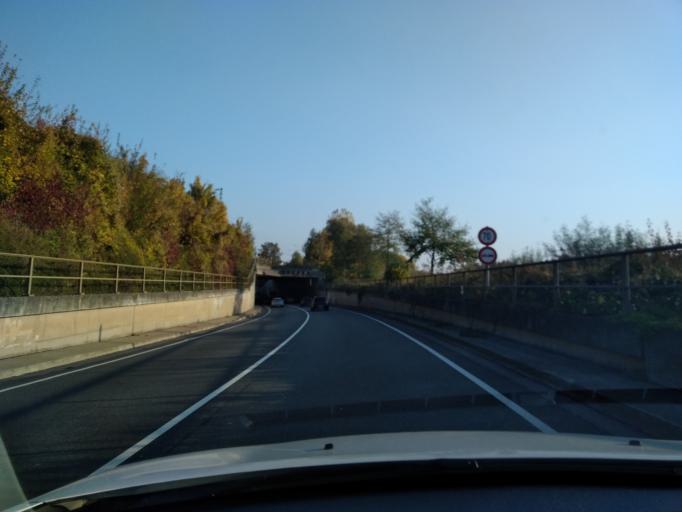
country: DE
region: Saarland
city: Kleinblittersdorf
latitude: 49.1535
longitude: 7.0354
